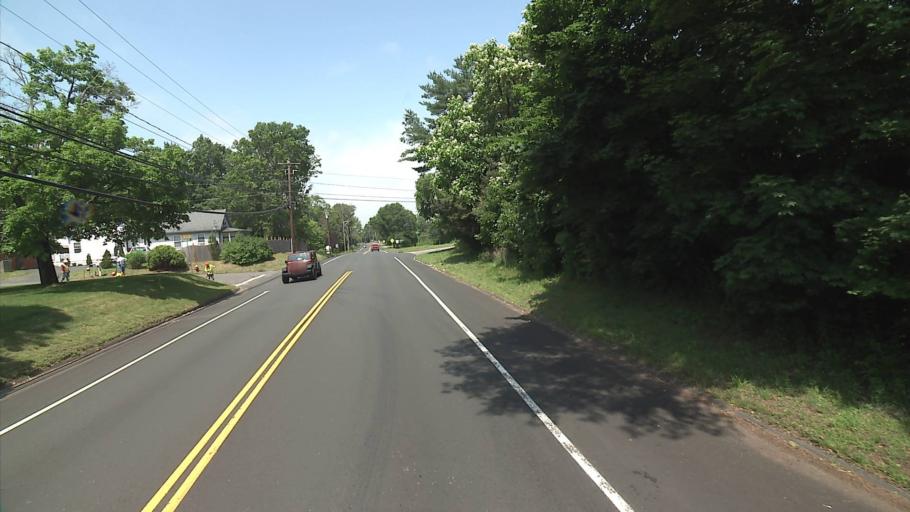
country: US
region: Connecticut
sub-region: Hartford County
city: Glastonbury Center
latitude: 41.7165
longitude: -72.5556
